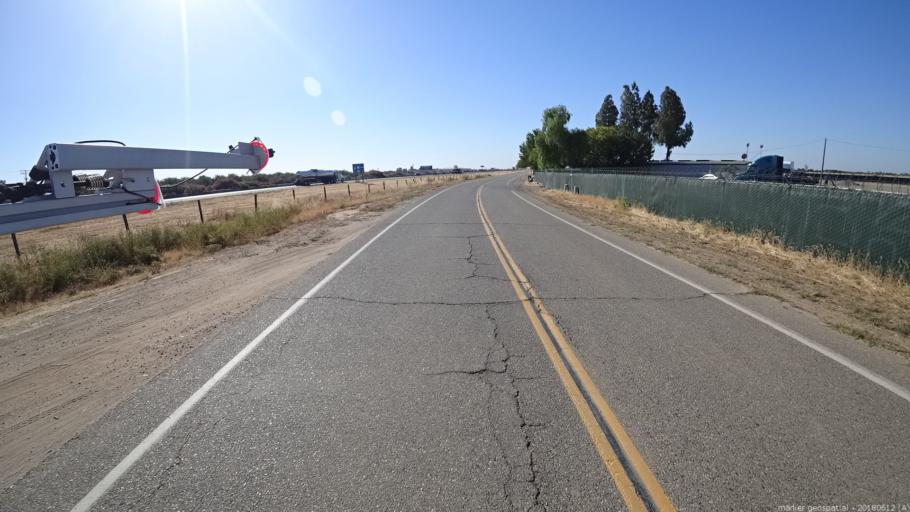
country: US
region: California
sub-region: Madera County
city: Madera Acres
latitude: 37.0105
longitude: -120.1191
